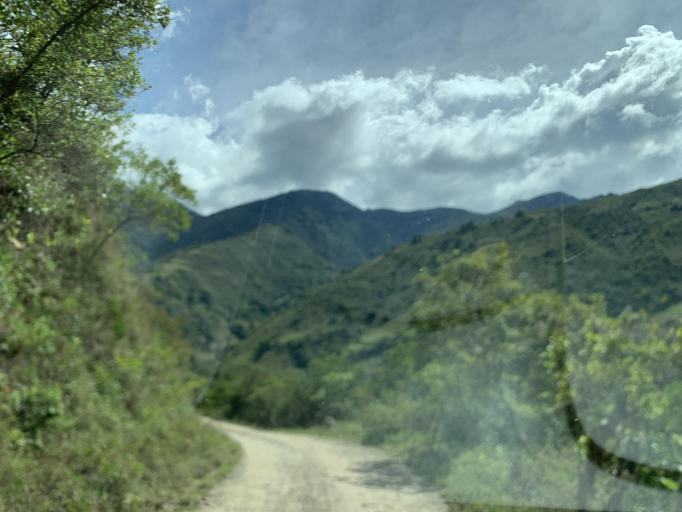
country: CO
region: Boyaca
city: Tipacoque
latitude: 6.4467
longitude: -72.7111
